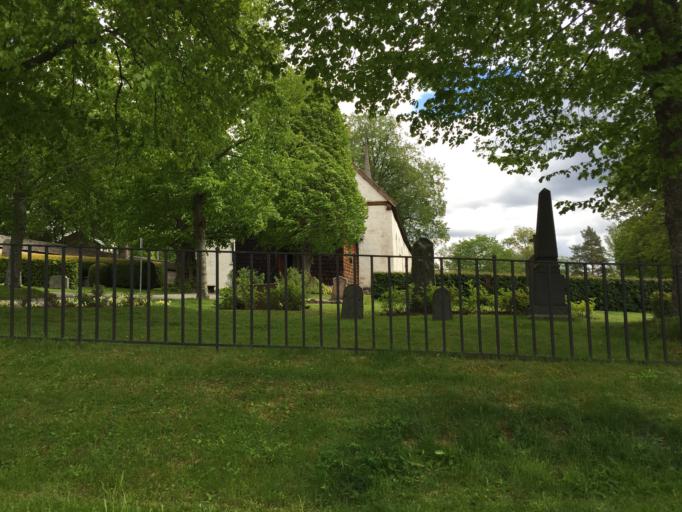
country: SE
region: OEstergoetland
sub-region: Finspangs Kommun
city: Finspang
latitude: 58.6751
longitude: 15.8433
